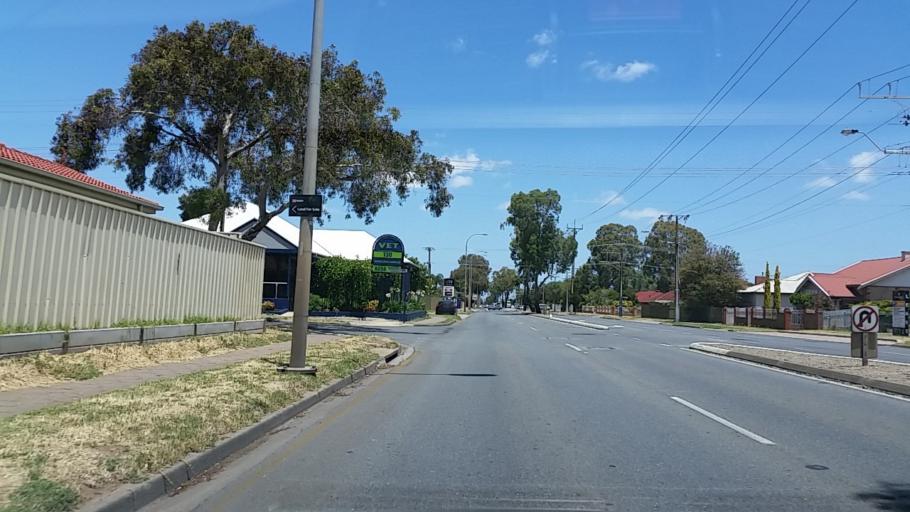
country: AU
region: South Australia
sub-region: Salisbury
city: Salisbury
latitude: -34.7657
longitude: 138.6386
